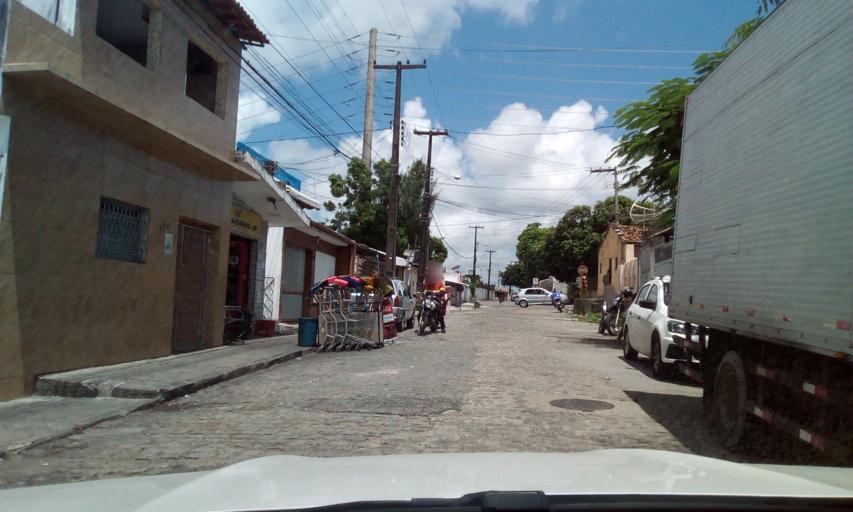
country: BR
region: Paraiba
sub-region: Joao Pessoa
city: Joao Pessoa
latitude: -7.1263
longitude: -34.8863
